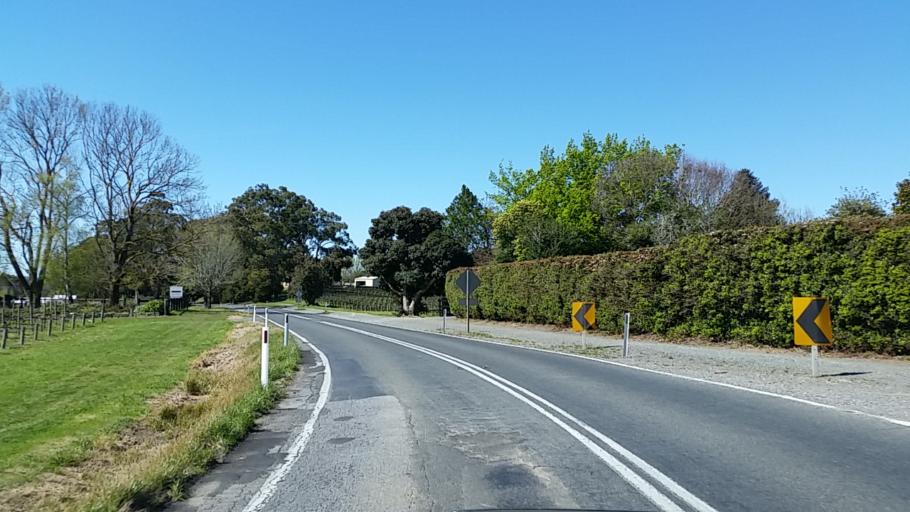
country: AU
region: South Australia
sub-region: Adelaide Hills
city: Bridgewater
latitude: -34.9585
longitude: 138.7392
